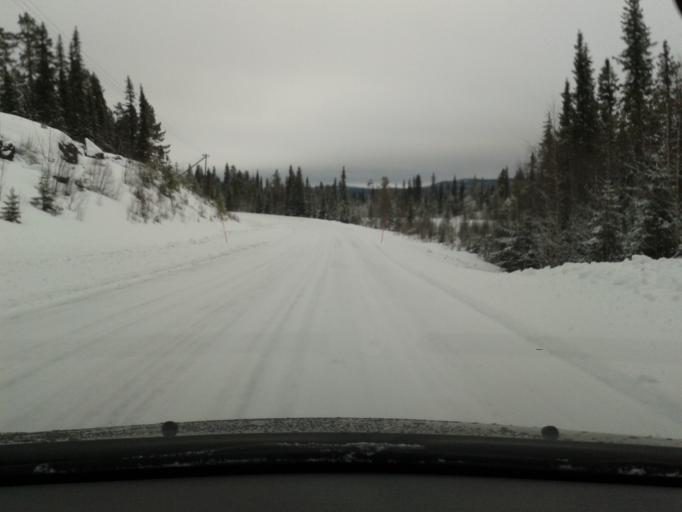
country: SE
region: Vaesterbotten
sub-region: Vilhelmina Kommun
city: Sjoberg
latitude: 65.2356
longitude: 15.8367
